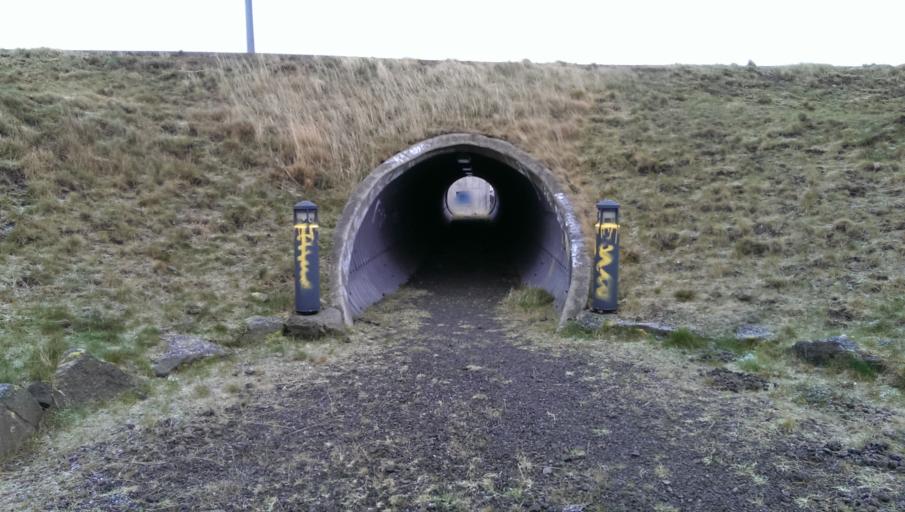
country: FO
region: Streymoy
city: Hoyvik
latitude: 62.0369
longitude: -6.7892
